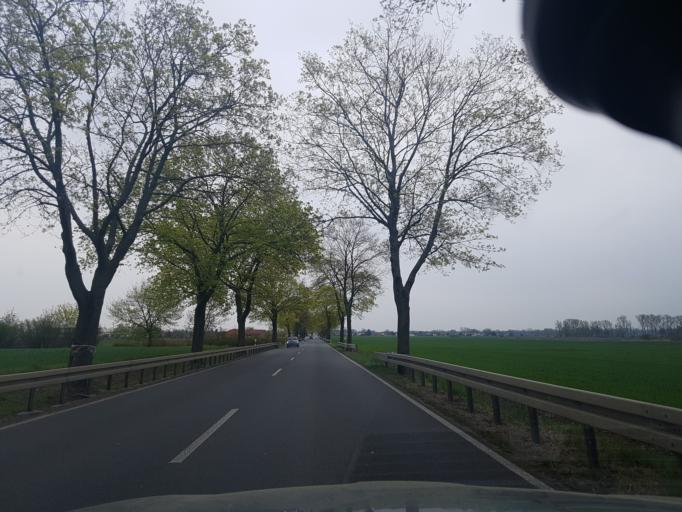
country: DE
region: Brandenburg
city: Plessa
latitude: 51.4668
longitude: 13.5980
